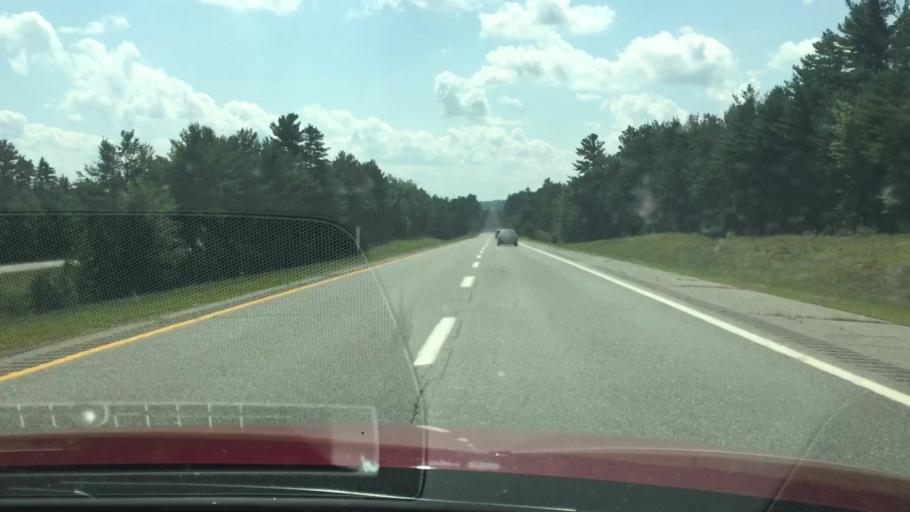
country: US
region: Maine
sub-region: Penobscot County
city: Medway
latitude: 45.4934
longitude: -68.5644
